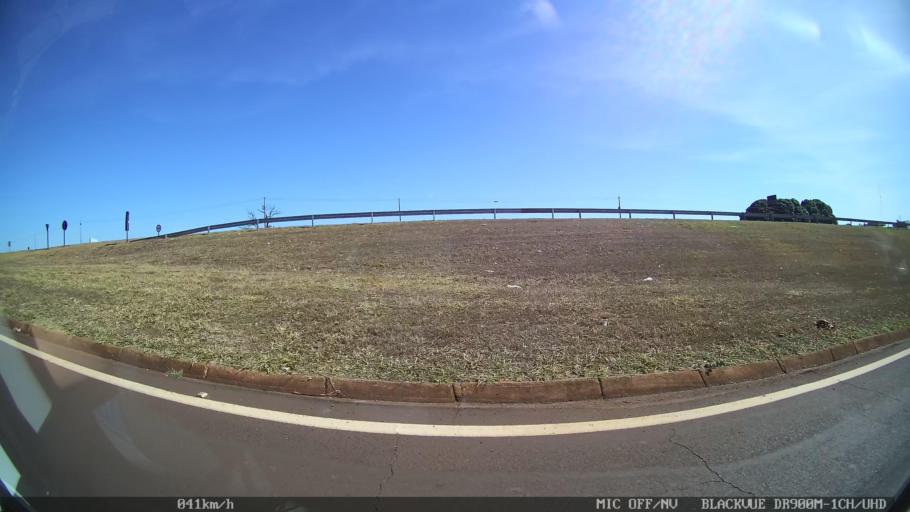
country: BR
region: Sao Paulo
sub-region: Barretos
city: Barretos
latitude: -20.5452
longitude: -48.5930
